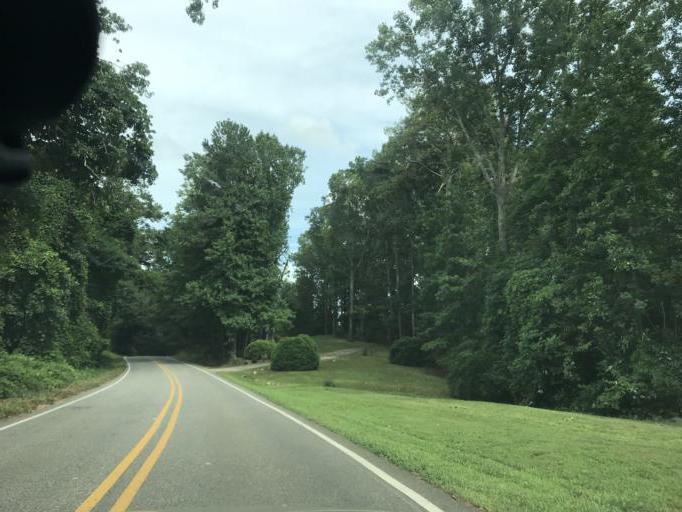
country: US
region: Georgia
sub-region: Cherokee County
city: Ball Ground
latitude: 34.3298
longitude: -84.2599
